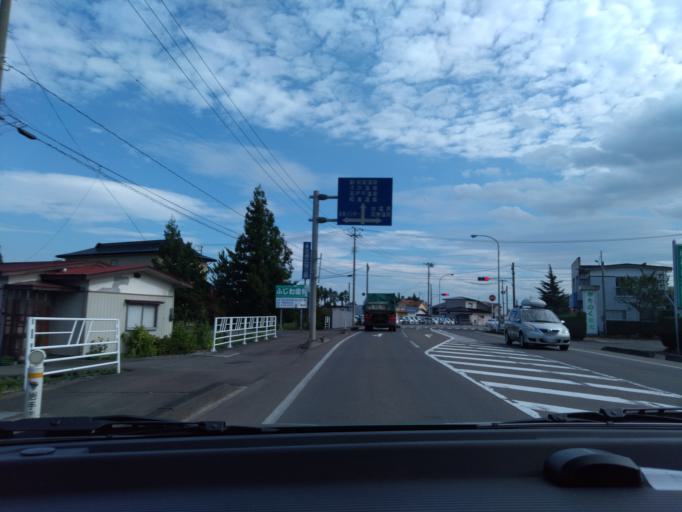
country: JP
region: Iwate
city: Hanamaki
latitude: 39.4450
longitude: 141.0986
